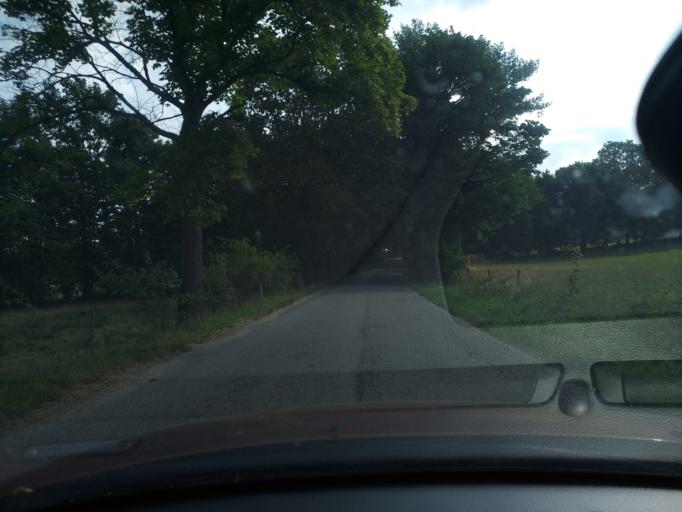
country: PL
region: Lower Silesian Voivodeship
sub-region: Powiat jeleniogorski
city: Stara Kamienica
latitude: 50.8818
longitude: 15.5595
